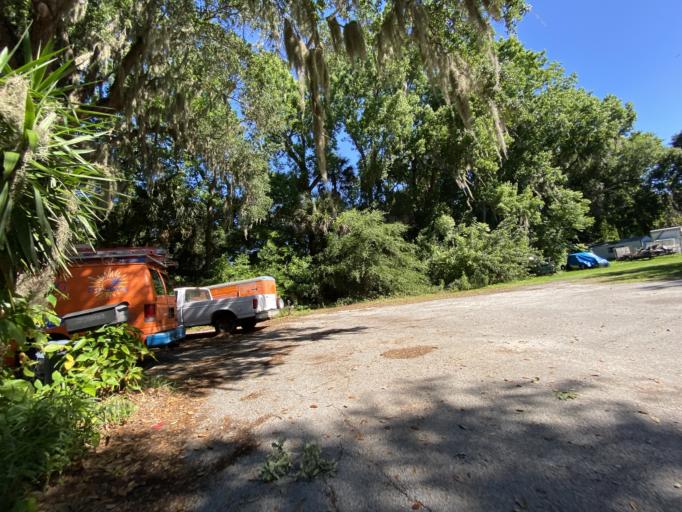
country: US
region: Florida
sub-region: Volusia County
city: Port Orange
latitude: 29.1432
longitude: -81.0022
